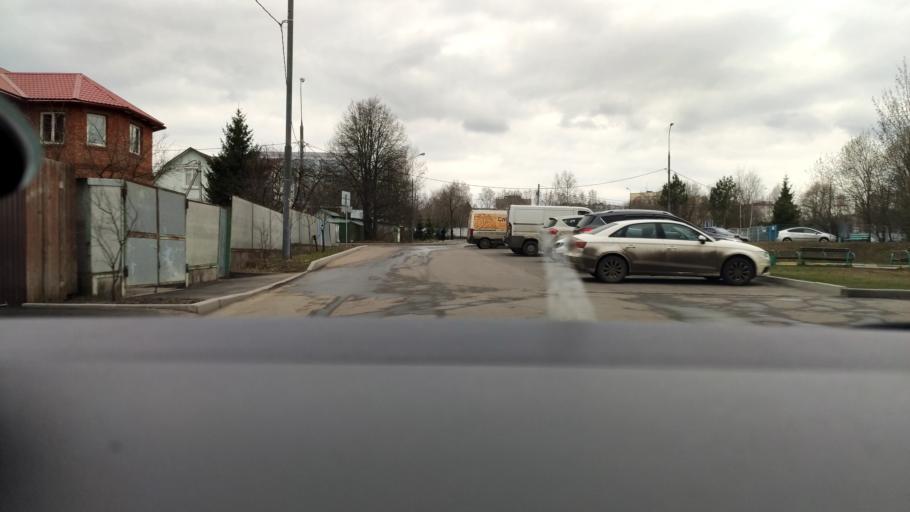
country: RU
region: Moskovskaya
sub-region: Leninskiy Rayon
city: Vnukovo
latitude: 55.6157
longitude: 37.2999
